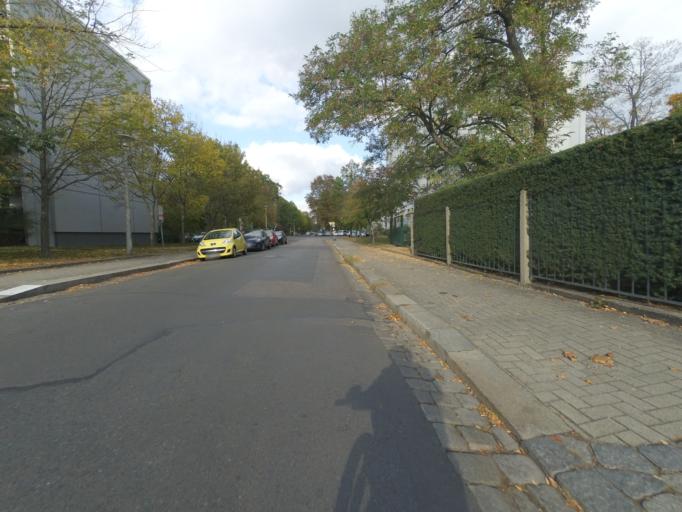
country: DE
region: Saxony
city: Albertstadt
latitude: 51.0532
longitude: 13.7876
